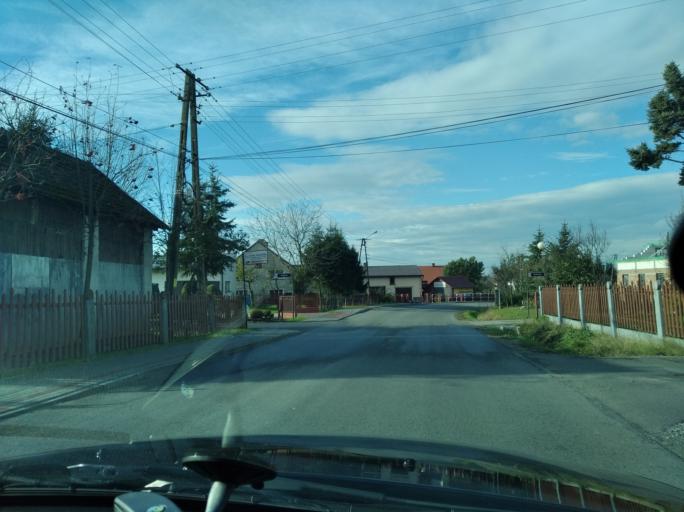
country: PL
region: Subcarpathian Voivodeship
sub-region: Powiat ropczycko-sedziszowski
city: Sedziszow Malopolski
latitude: 50.0829
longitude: 21.7179
